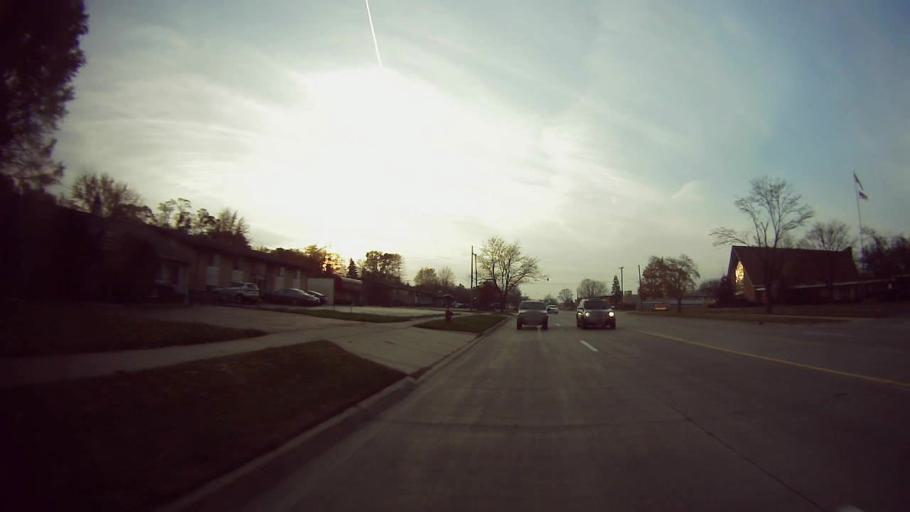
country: US
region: Michigan
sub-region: Oakland County
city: Lathrup Village
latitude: 42.5025
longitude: -83.2192
